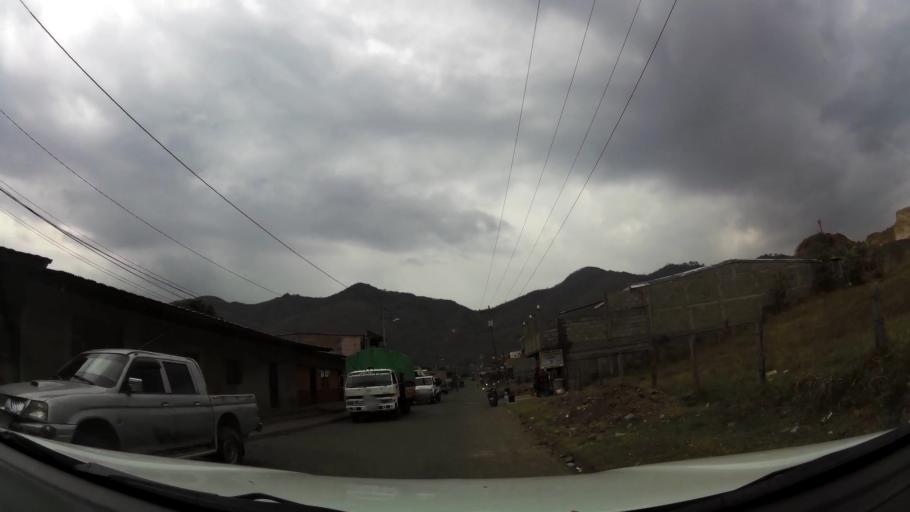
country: NI
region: Jinotega
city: Jinotega
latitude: 13.0977
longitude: -85.9995
